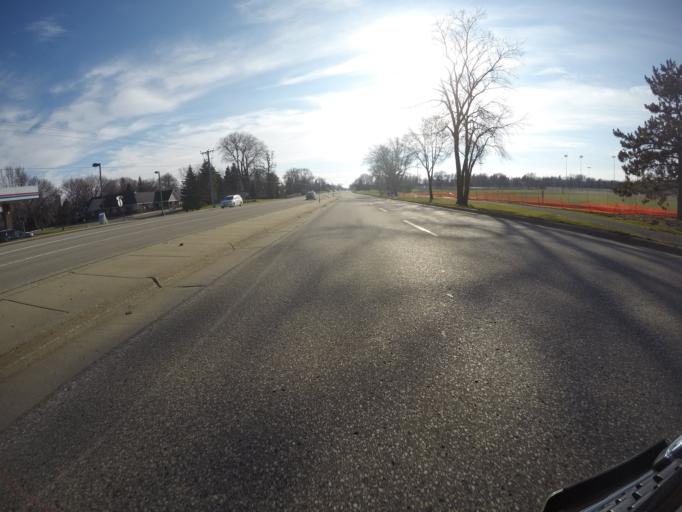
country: US
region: Minnesota
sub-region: Hennepin County
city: Eden Prairie
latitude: 44.8685
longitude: -93.4857
